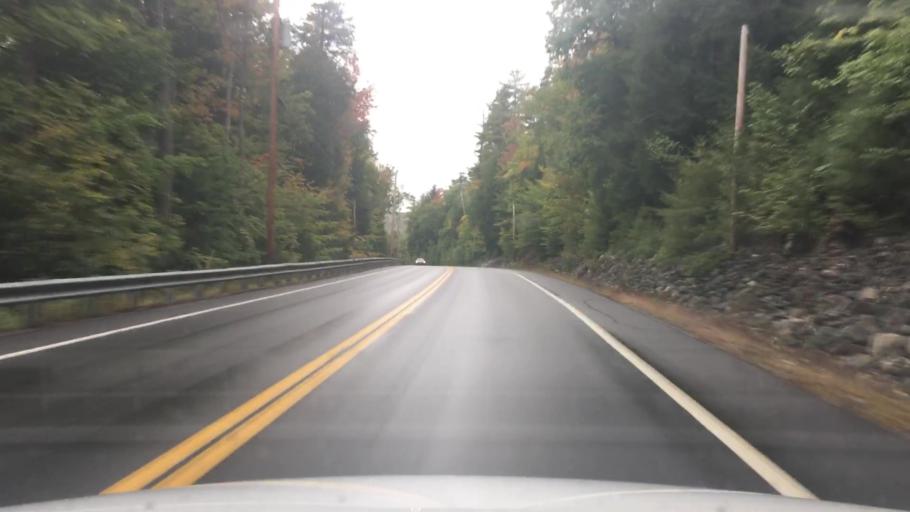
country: US
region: Maine
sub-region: Kennebec County
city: Rome
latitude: 44.5439
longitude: -69.8924
